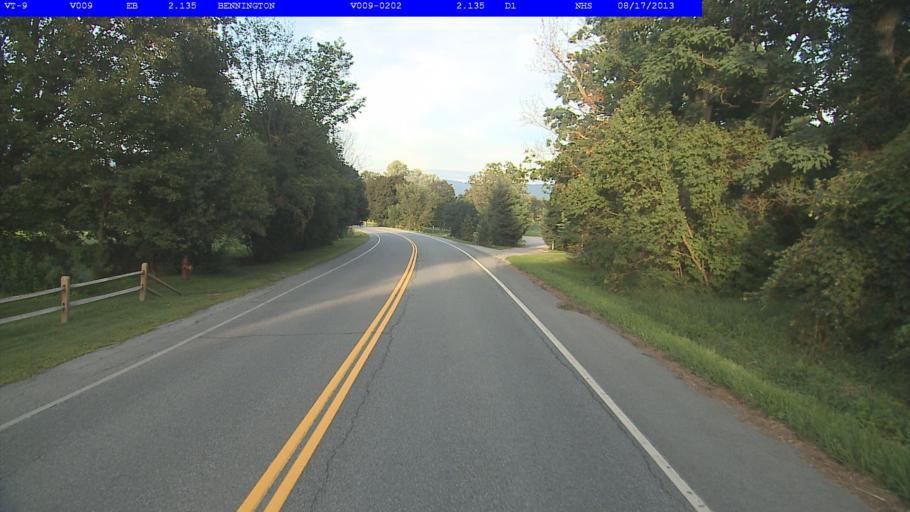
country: US
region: Vermont
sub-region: Bennington County
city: Bennington
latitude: 42.8801
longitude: -73.2370
